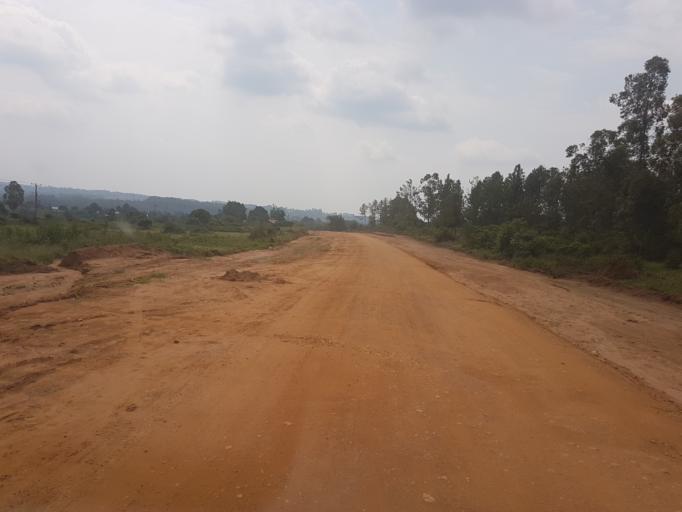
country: UG
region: Western Region
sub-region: Kanungu District
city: Ntungamo
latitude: -0.8113
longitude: 29.7061
